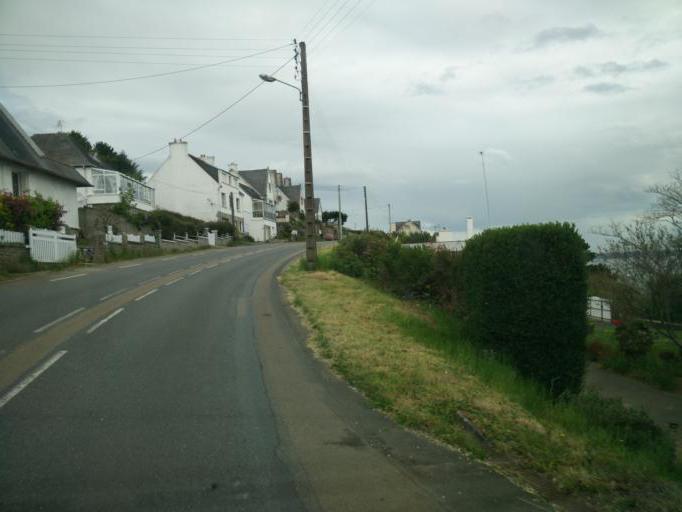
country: FR
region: Brittany
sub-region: Departement du Finistere
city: Locquirec
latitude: 48.6817
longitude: -3.6560
